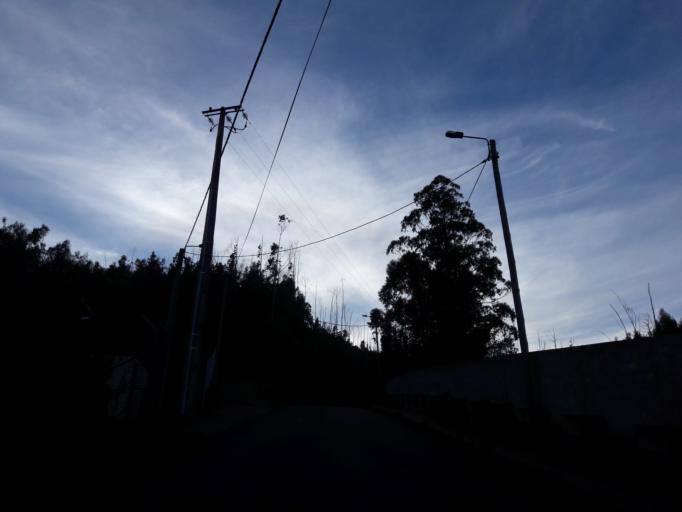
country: PT
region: Madeira
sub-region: Santa Cruz
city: Camacha
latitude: 32.6869
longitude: -16.8610
